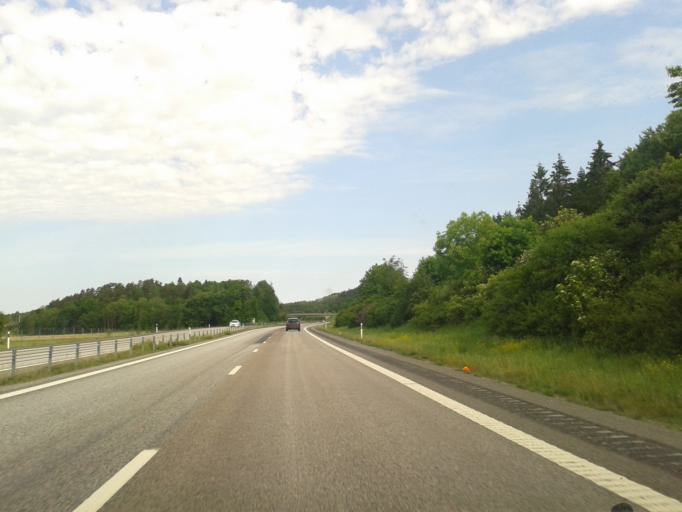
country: SE
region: Vaestra Goetaland
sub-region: Munkedals Kommun
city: Munkedal
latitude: 58.5369
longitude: 11.5304
